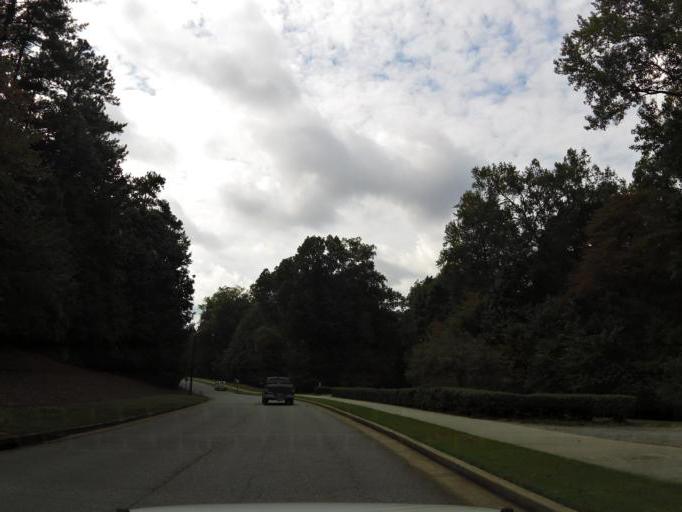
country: US
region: Georgia
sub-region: Cobb County
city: Kennesaw
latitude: 34.0522
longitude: -84.6302
